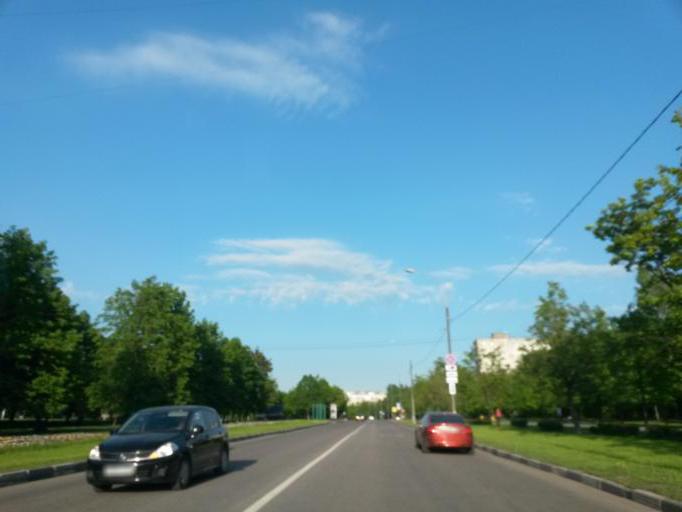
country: RU
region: Moskovskaya
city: Biryulevo Zapadnoye
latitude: 55.5868
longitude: 37.6507
